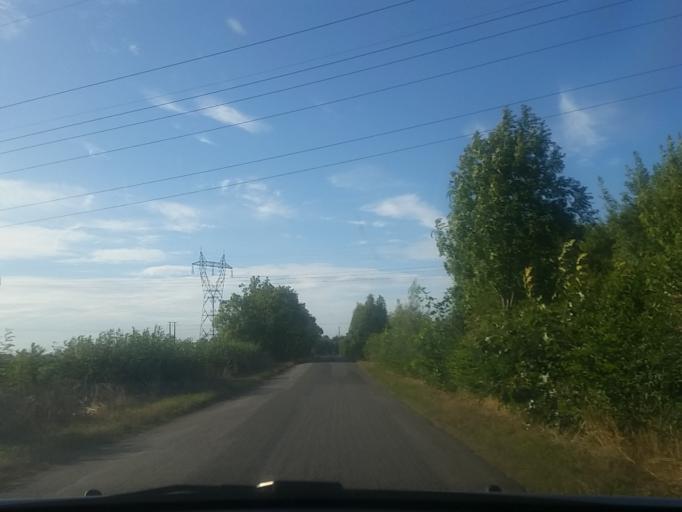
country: FR
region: Pays de la Loire
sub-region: Departement de la Loire-Atlantique
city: Bouguenais
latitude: 47.1820
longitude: -1.6334
